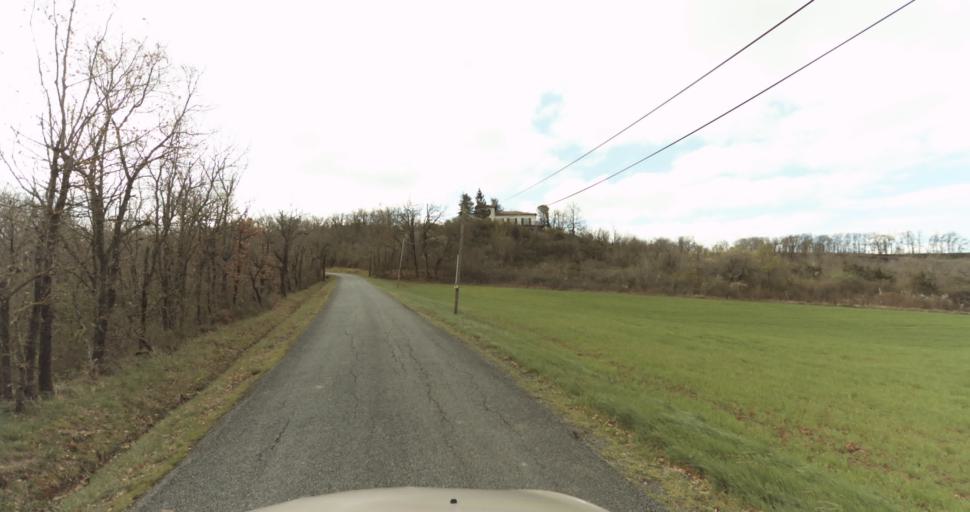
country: FR
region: Midi-Pyrenees
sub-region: Departement du Tarn
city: Puygouzon
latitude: 43.8743
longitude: 2.1942
